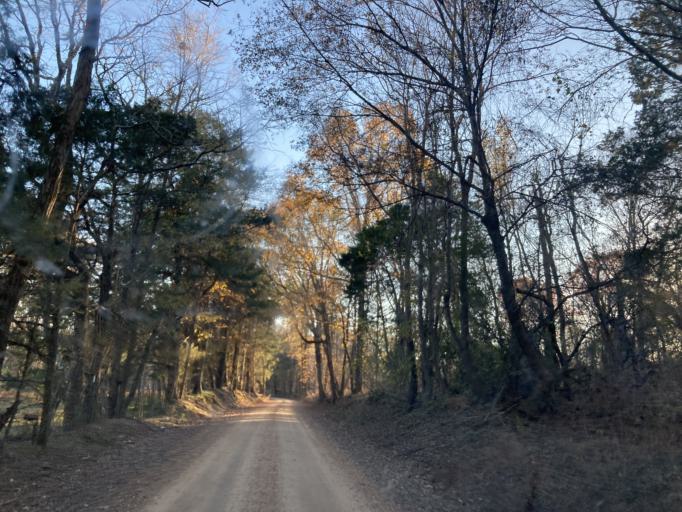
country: US
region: Mississippi
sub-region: Yazoo County
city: Yazoo City
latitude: 32.9447
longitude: -90.2857
